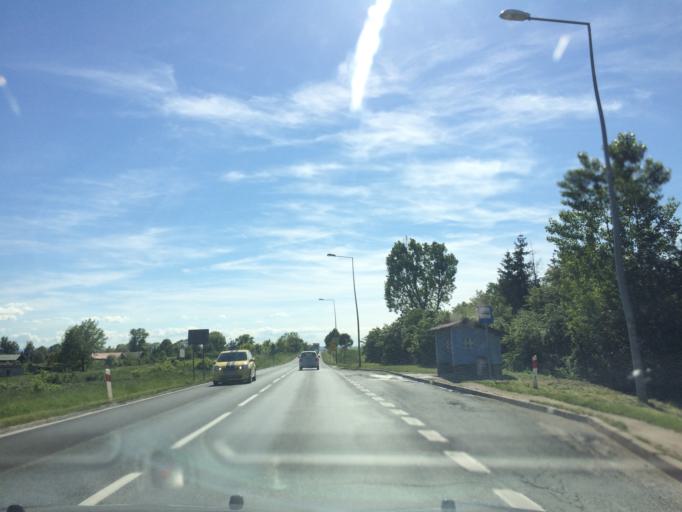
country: PL
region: Lower Silesian Voivodeship
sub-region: Powiat wroclawski
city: Sobotka
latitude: 50.8978
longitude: 16.6225
